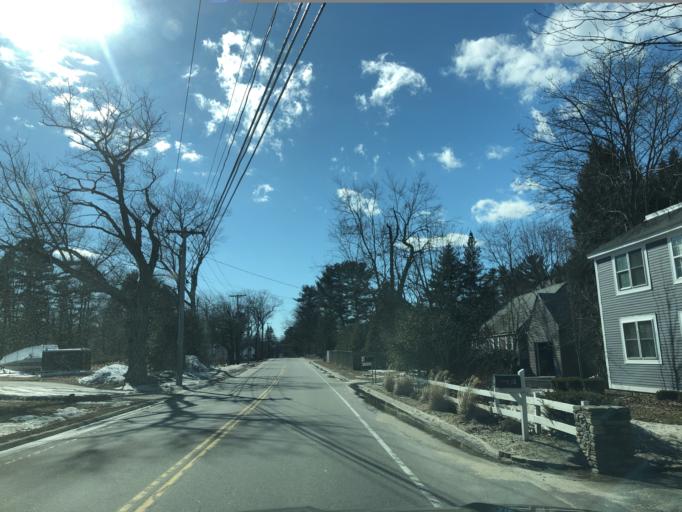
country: US
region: Maine
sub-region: Cumberland County
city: Falmouth
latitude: 43.7131
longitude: -70.2712
